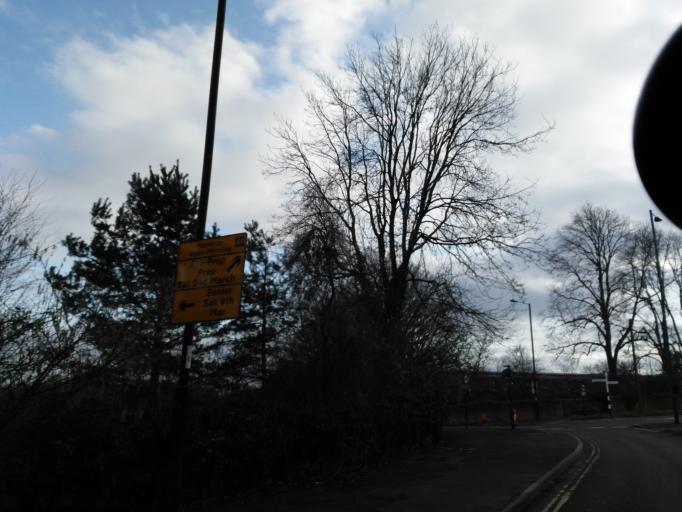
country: GB
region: England
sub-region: Bath and North East Somerset
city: Freshford
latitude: 51.3666
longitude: -2.3189
